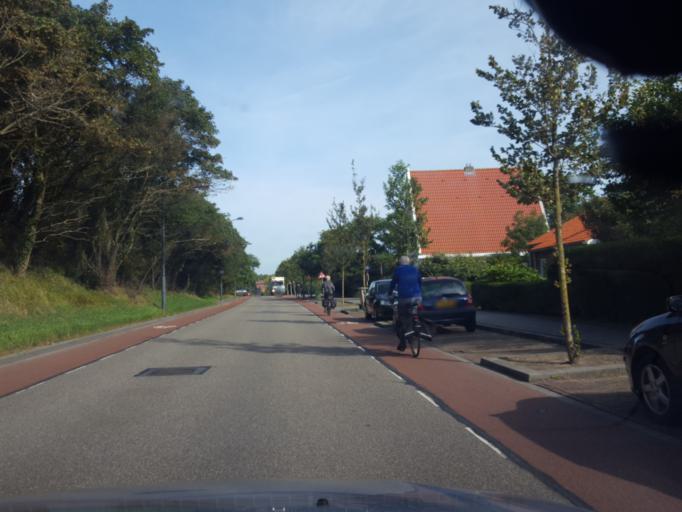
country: NL
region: Zeeland
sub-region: Gemeente Vlissingen
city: Vlissingen
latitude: 51.4488
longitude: 3.5622
